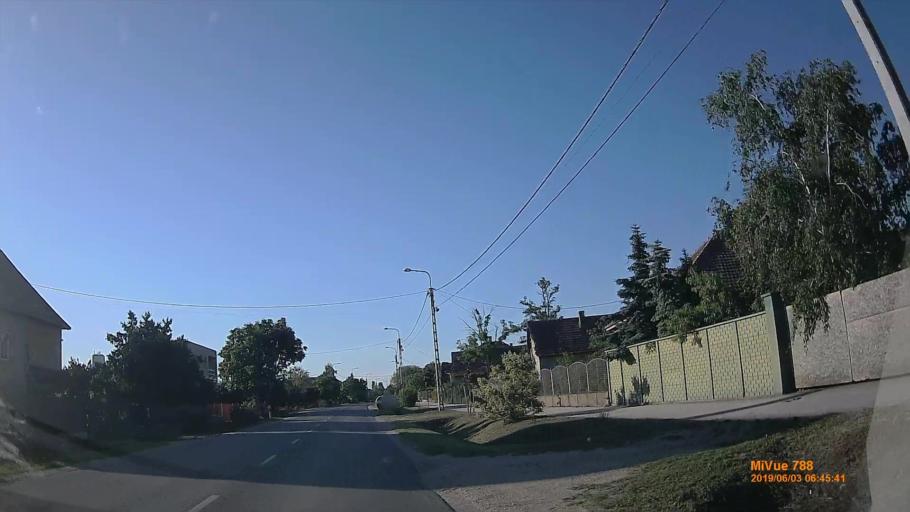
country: HU
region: Pest
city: Bugyi
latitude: 47.2361
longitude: 19.1384
